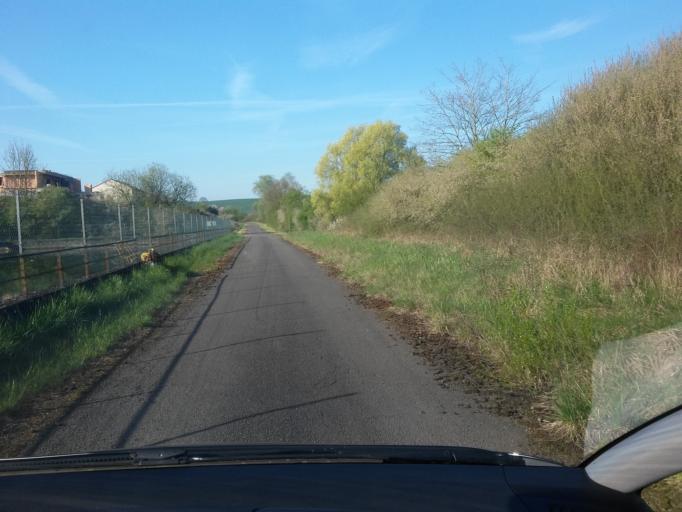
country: FR
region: Lorraine
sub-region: Departement de la Meuse
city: Montmedy
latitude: 49.5189
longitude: 5.3952
